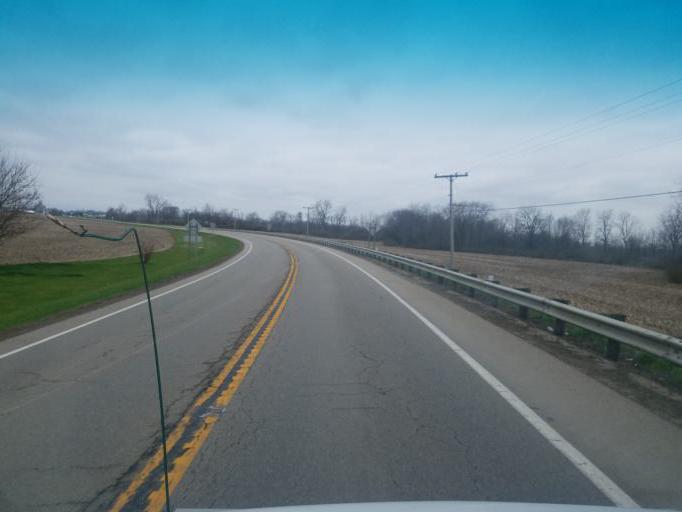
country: US
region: Ohio
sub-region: Van Wert County
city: Van Wert
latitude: 40.8994
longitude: -84.5756
